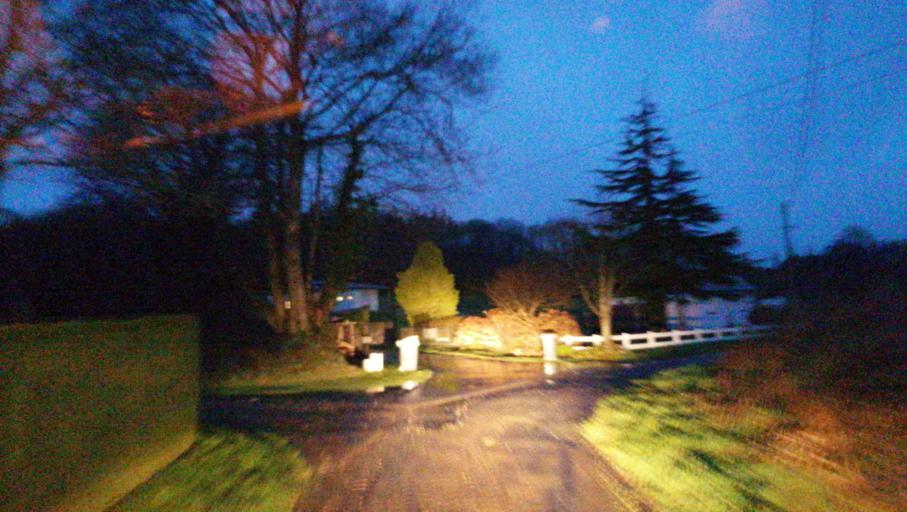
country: FR
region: Brittany
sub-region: Departement des Cotes-d'Armor
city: Plouagat
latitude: 48.4813
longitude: -2.9688
